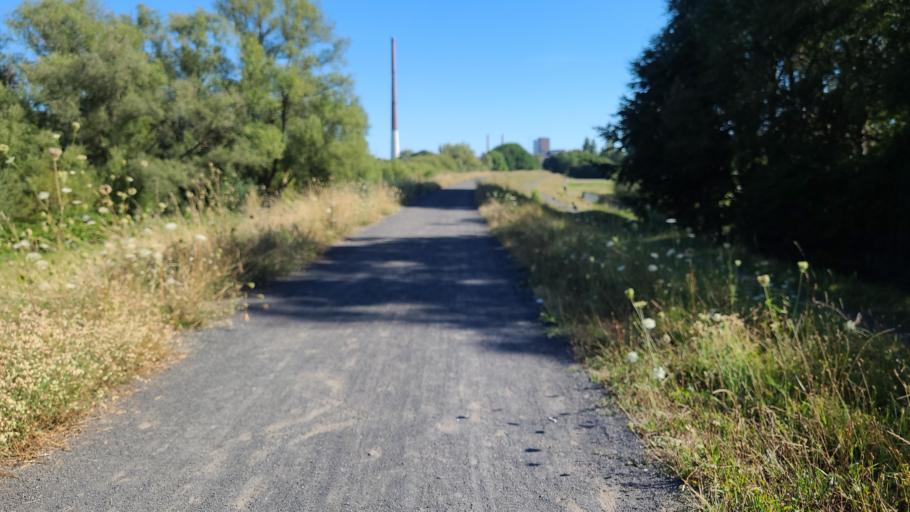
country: DE
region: North Rhine-Westphalia
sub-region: Regierungsbezirk Koln
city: Leverkusen
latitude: 51.0034
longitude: 6.9717
